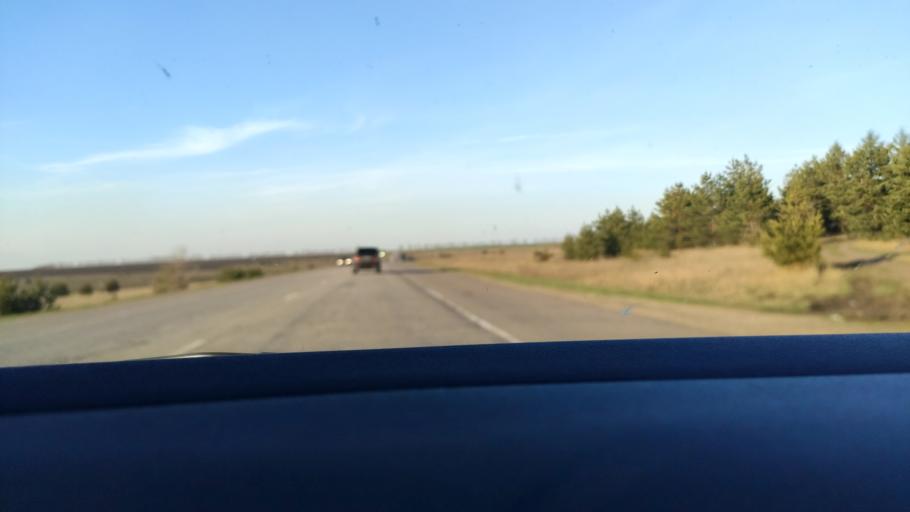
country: RU
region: Voronezj
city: Kolodeznyy
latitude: 51.3824
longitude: 39.2191
